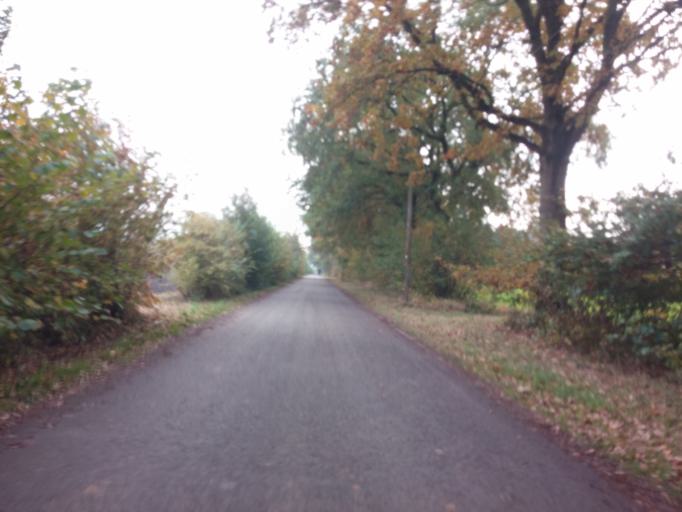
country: DE
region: North Rhine-Westphalia
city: Dorsten
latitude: 51.6355
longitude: 6.9800
